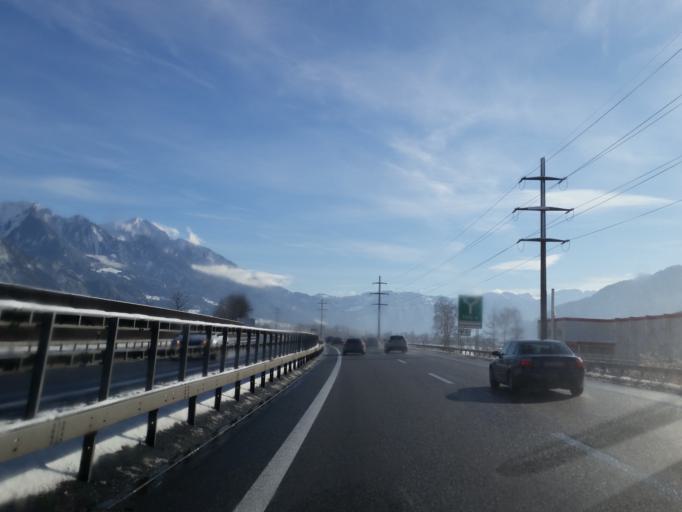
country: CH
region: Saint Gallen
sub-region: Wahlkreis Sarganserland
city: Sargans
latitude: 47.0403
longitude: 9.4402
